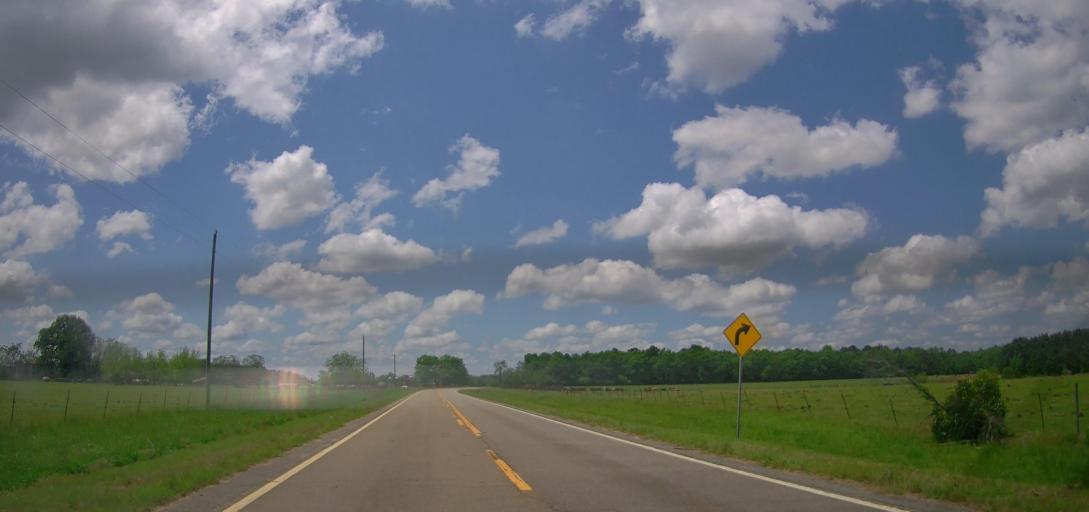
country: US
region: Georgia
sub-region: Dodge County
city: Chester
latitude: 32.5436
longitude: -83.1822
